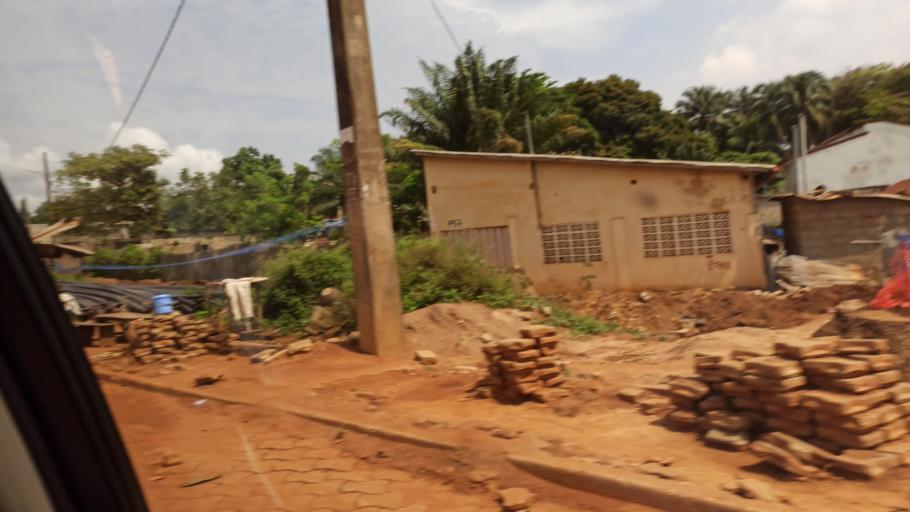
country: BJ
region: Queme
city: Porto-Novo
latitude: 6.4768
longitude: 2.5943
